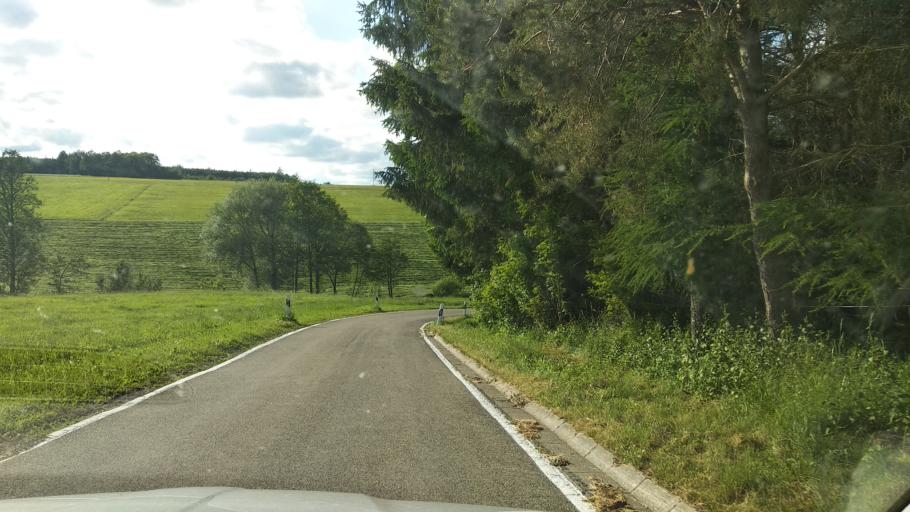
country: DE
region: Baden-Wuerttemberg
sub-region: Tuebingen Region
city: Aitrach
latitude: 47.9508
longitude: 10.0420
